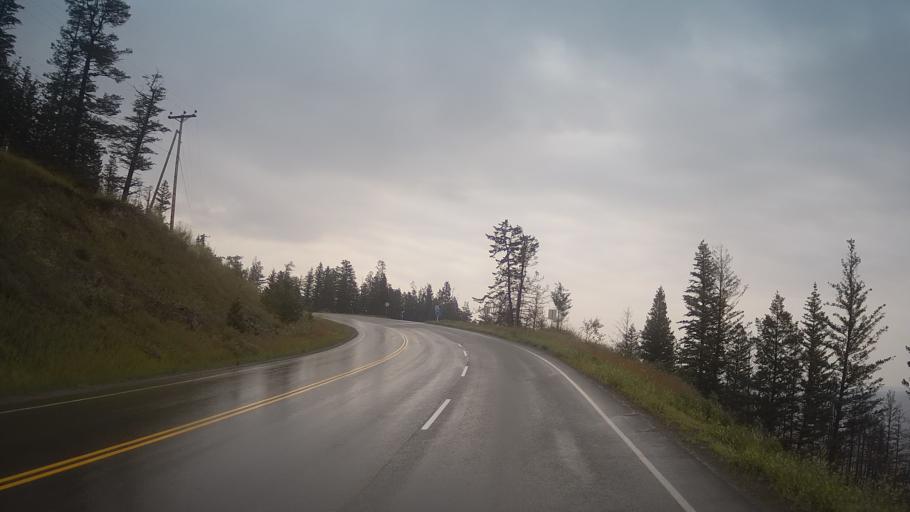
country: CA
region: British Columbia
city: Hanceville
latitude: 51.9373
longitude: -122.9902
